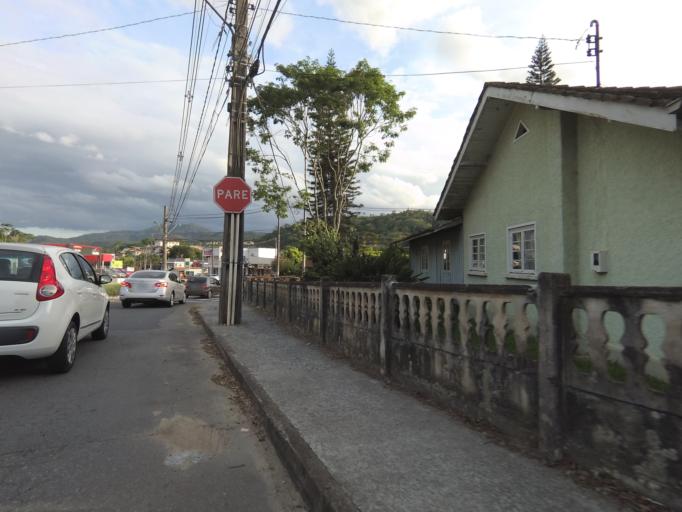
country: BR
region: Santa Catarina
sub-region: Blumenau
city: Blumenau
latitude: -26.9081
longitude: -49.1222
